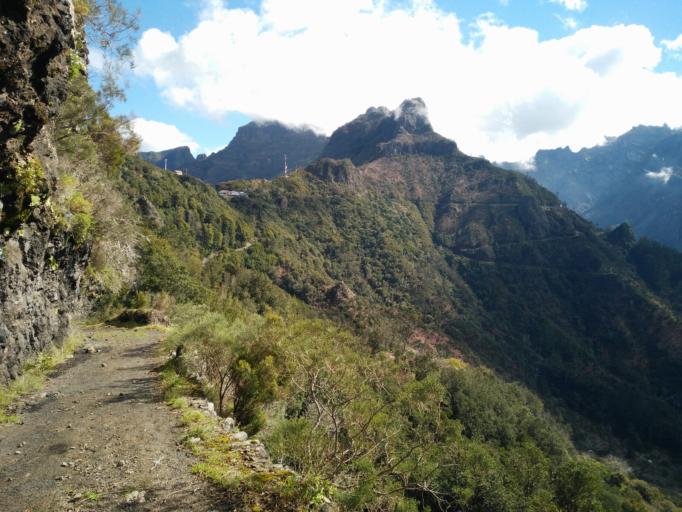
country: PT
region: Madeira
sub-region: Sao Vicente
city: Sao Vicente
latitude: 32.7517
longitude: -17.0265
